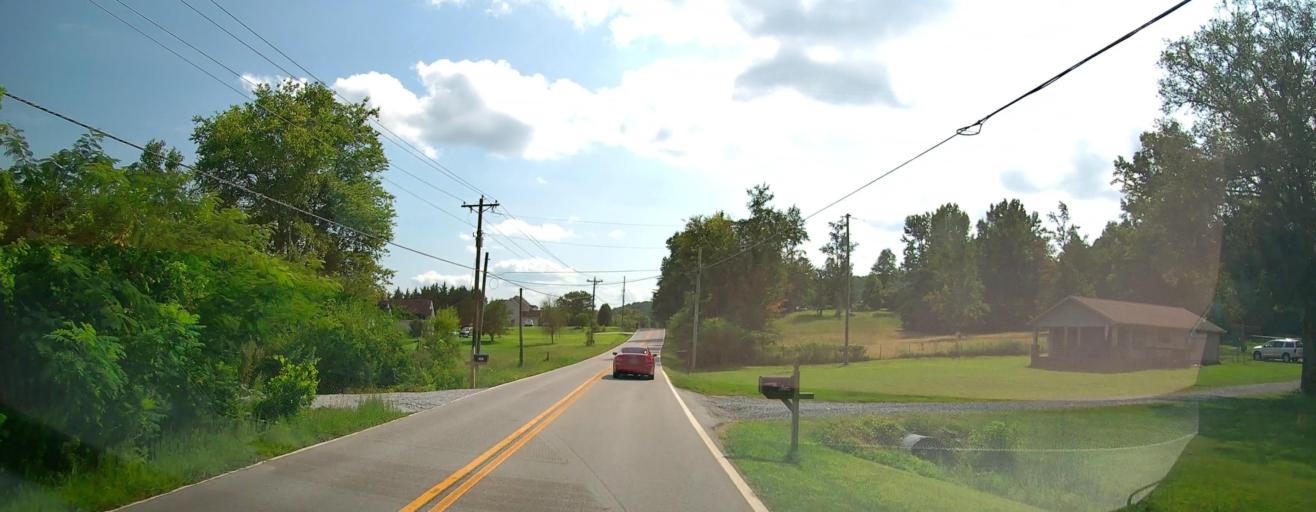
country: US
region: Georgia
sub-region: Catoosa County
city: Ringgold
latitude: 34.9376
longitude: -85.0829
